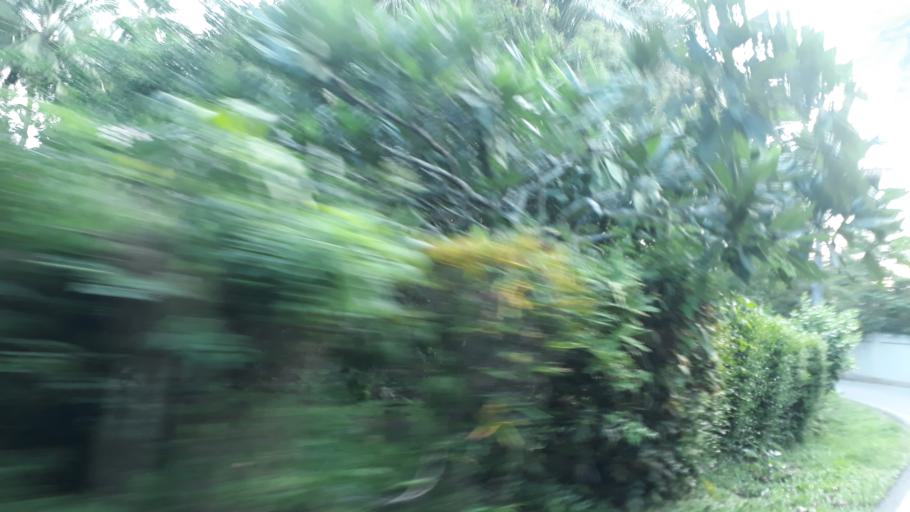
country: LK
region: Western
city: Gampaha
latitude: 7.1013
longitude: 79.9840
